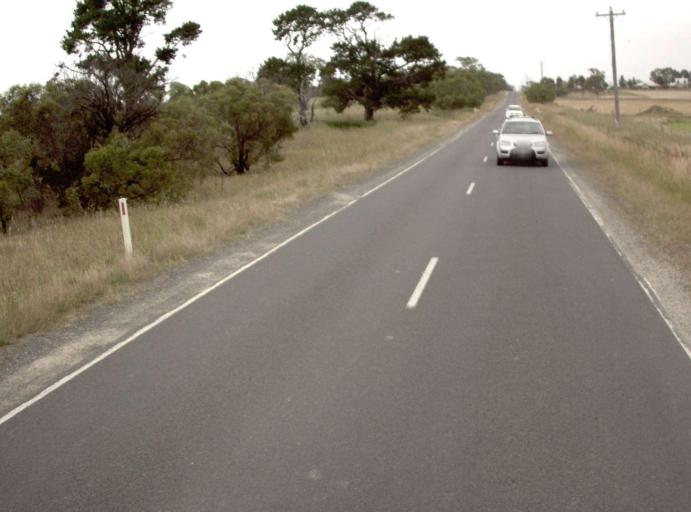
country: AU
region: Victoria
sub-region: Wellington
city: Heyfield
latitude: -38.0338
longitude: 146.7663
